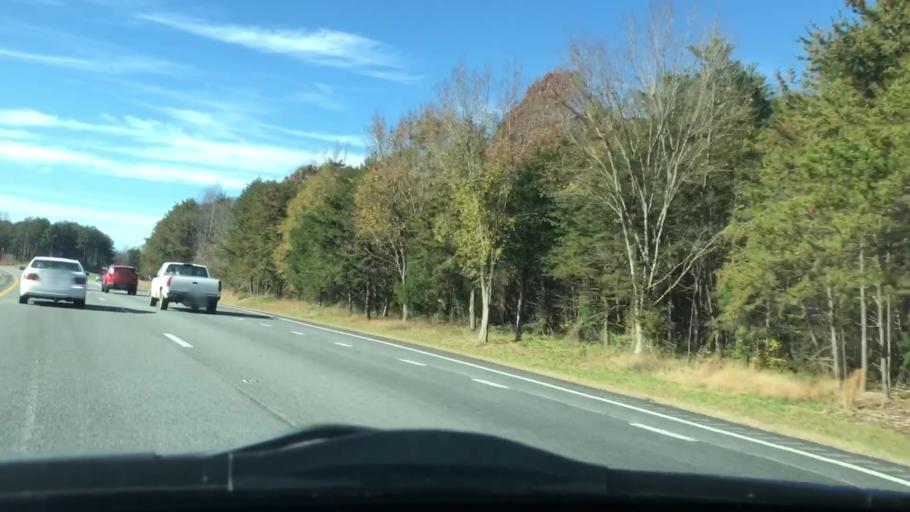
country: US
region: North Carolina
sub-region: Guilford County
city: High Point
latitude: 36.0242
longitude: -80.0537
